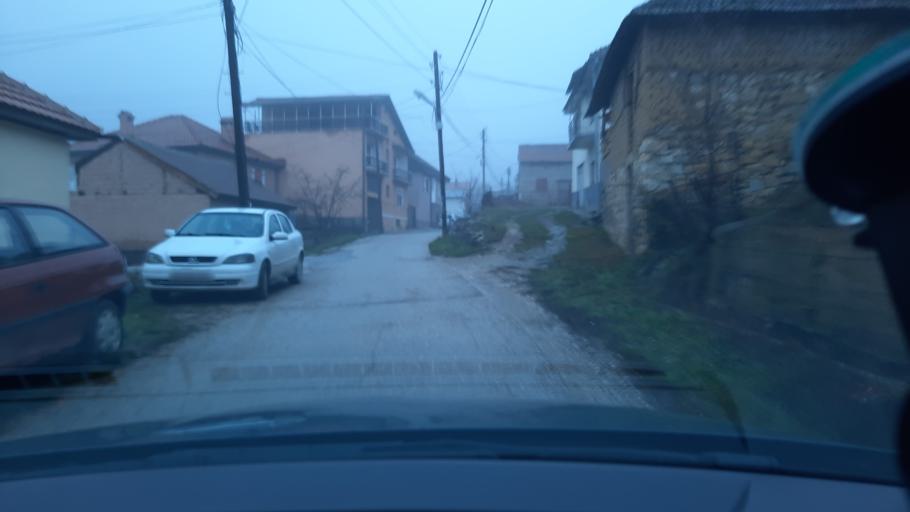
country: MK
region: Vrapciste
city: Vrapciste
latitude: 41.8392
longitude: 20.8806
